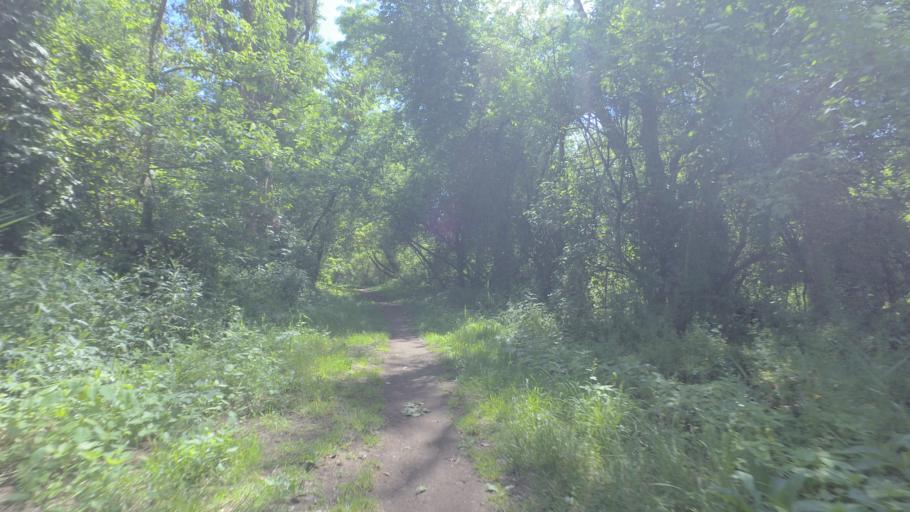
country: DE
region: Brandenburg
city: Rangsdorf
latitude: 52.2761
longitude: 13.4139
